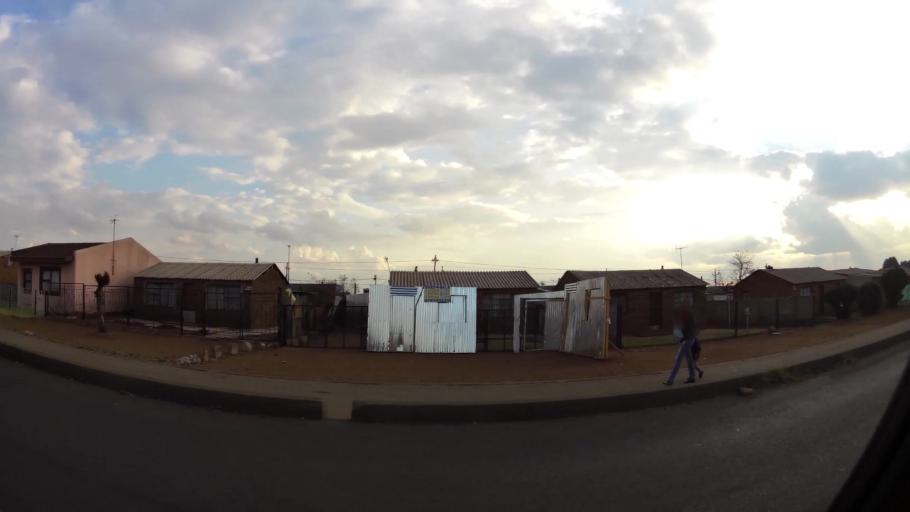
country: ZA
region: Gauteng
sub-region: City of Johannesburg Metropolitan Municipality
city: Orange Farm
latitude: -26.5777
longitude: 27.8410
